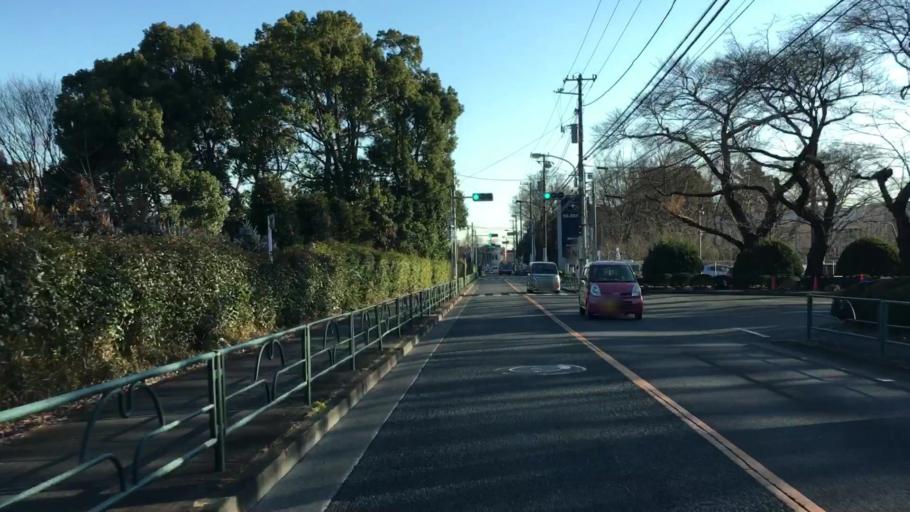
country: JP
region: Tokyo
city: Mitaka-shi
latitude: 35.6865
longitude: 139.5384
